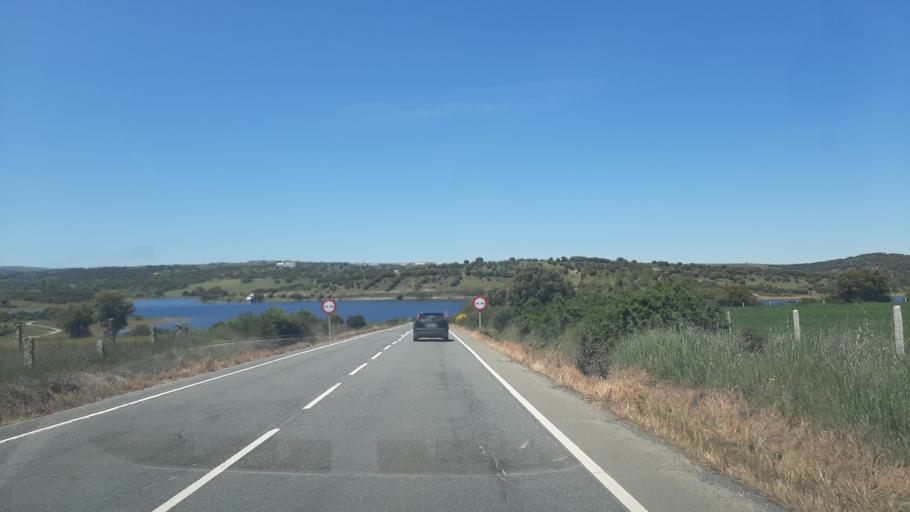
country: ES
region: Castille and Leon
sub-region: Provincia de Salamanca
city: Guijo de Avila
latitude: 40.5499
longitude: -5.6226
